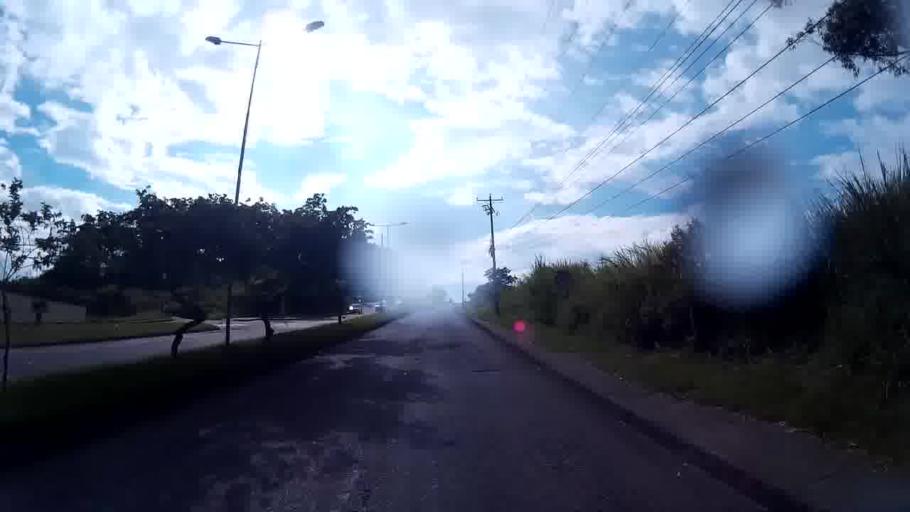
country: CO
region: Quindio
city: Calarca
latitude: 4.5618
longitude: -75.6507
